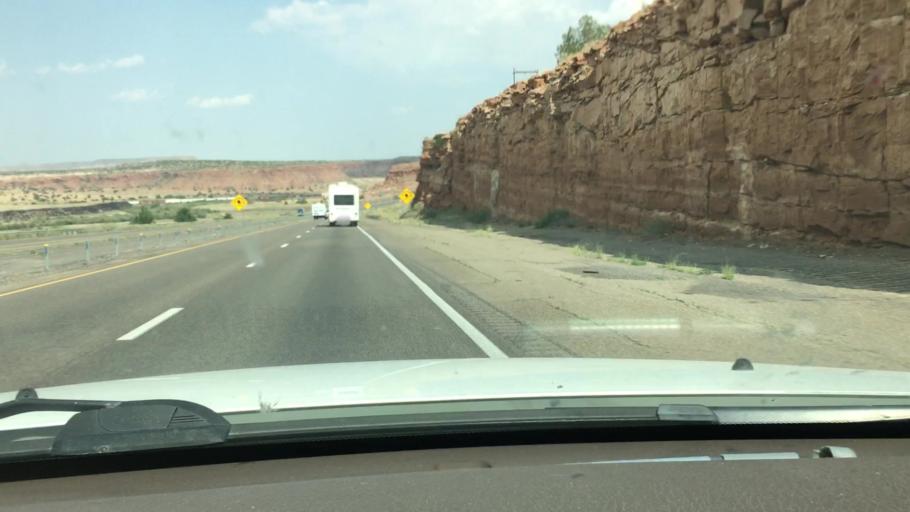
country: US
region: New Mexico
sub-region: Cibola County
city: Laguna
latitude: 35.0360
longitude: -107.3495
